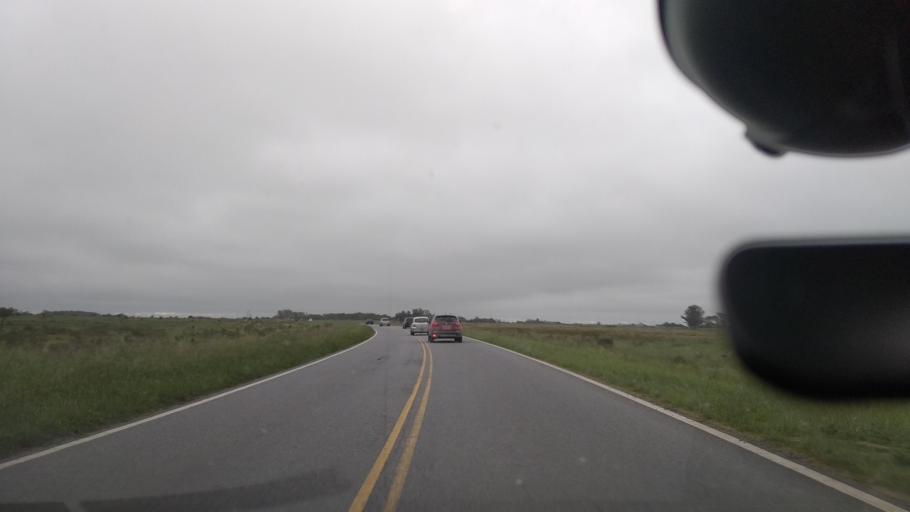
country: AR
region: Buenos Aires
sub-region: Partido de Magdalena
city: Magdalena
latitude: -35.2464
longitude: -57.6722
